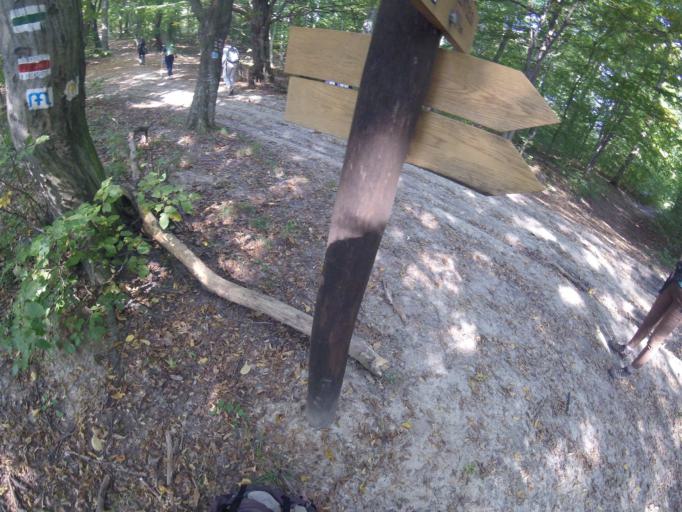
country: HU
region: Komarom-Esztergom
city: Kesztolc
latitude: 47.7385
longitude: 18.8450
